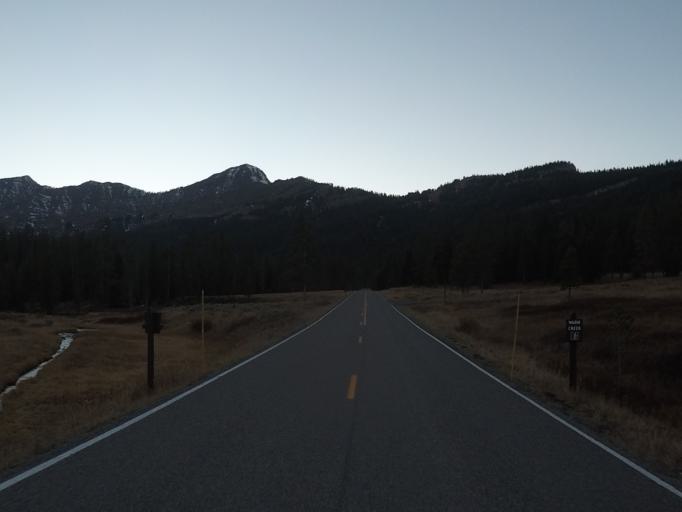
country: US
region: Montana
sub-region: Stillwater County
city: Absarokee
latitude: 45.0044
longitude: -110.0324
